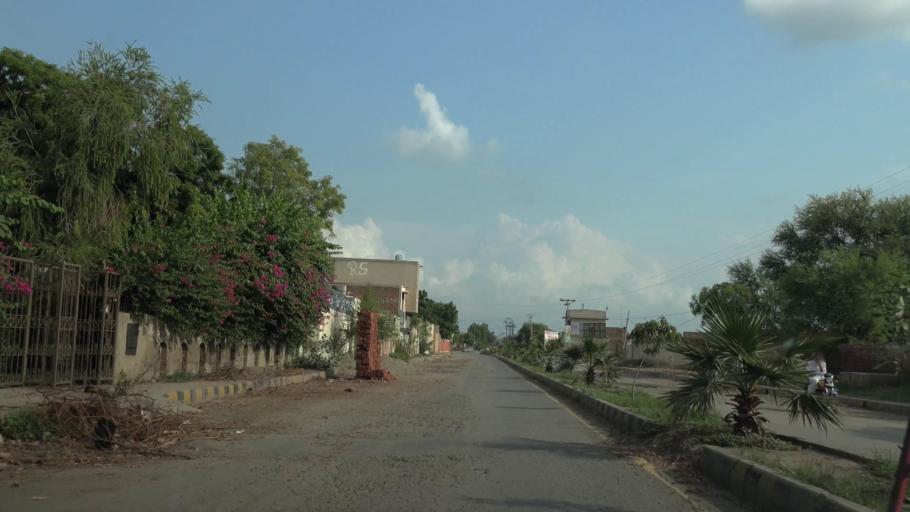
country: PK
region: Punjab
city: Nankana Sahib
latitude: 31.4519
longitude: 73.6966
